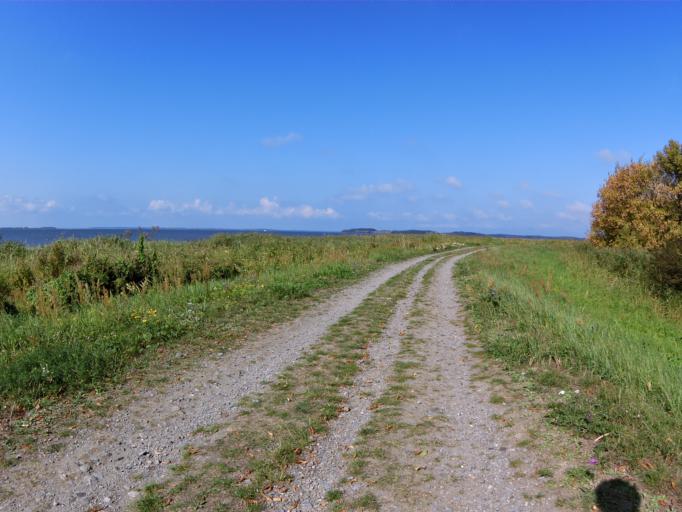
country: DE
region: Mecklenburg-Vorpommern
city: Loddin
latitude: 53.9925
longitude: 14.0475
